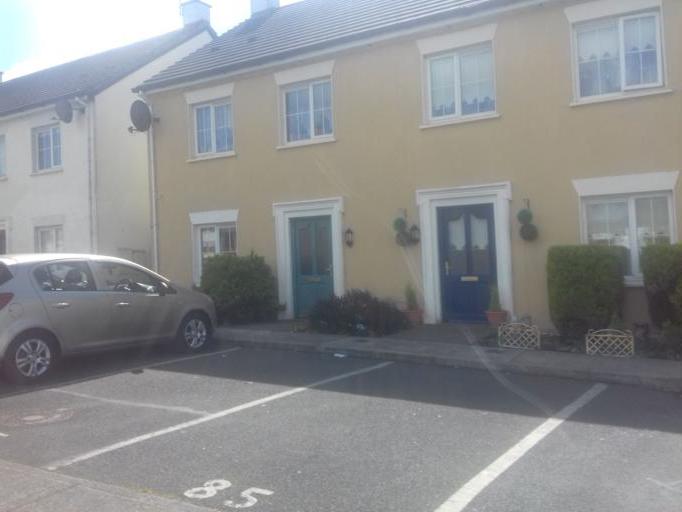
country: IE
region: Leinster
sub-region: Laois
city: Portlaoise
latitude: 53.0420
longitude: -7.2998
